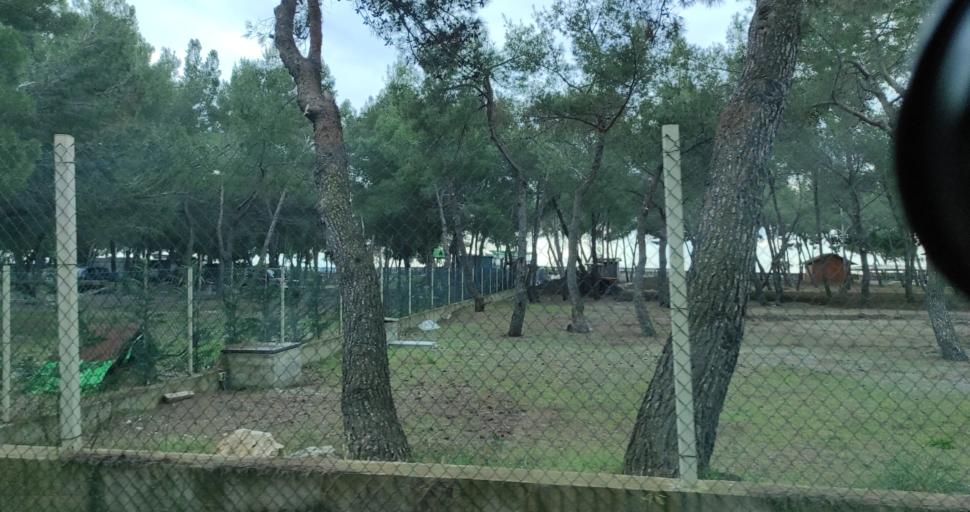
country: AL
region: Lezhe
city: Shengjin
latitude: 41.8202
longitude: 19.5640
